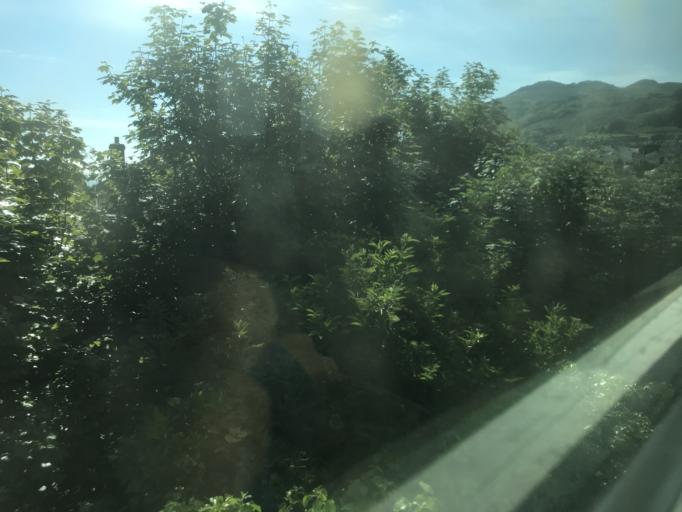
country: IE
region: Leinster
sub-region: Wicklow
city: Bray
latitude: 53.1979
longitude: -6.0964
